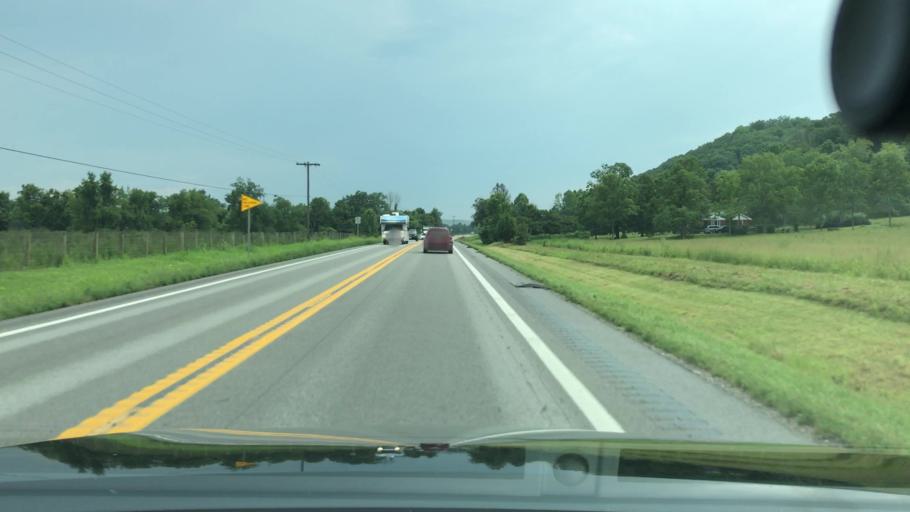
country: US
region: West Virginia
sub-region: Putnam County
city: Buffalo
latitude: 38.6543
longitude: -81.9698
